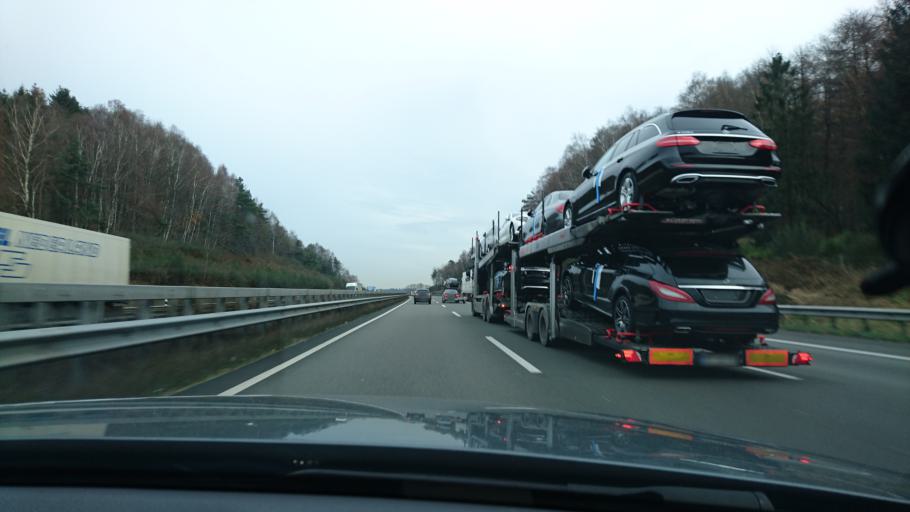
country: DE
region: Lower Saxony
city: Wallenhorst
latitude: 52.3706
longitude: 8.0433
